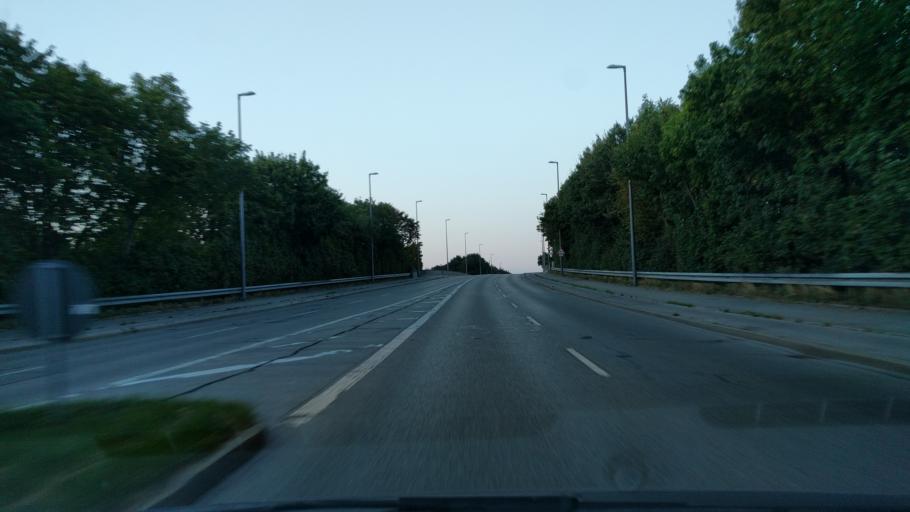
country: DE
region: Bavaria
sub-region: Upper Bavaria
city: Bogenhausen
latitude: 48.1266
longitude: 11.6553
